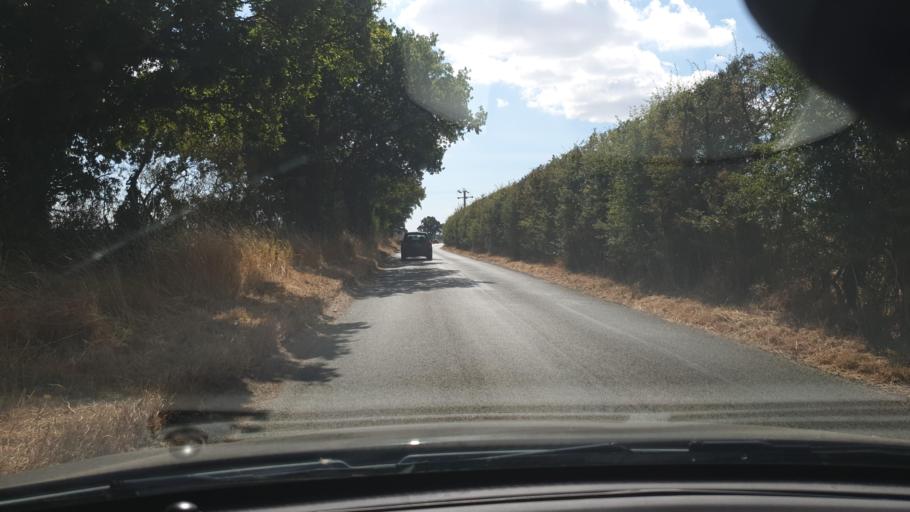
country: GB
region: England
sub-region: Essex
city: Great Bentley
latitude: 51.8544
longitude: 1.0411
